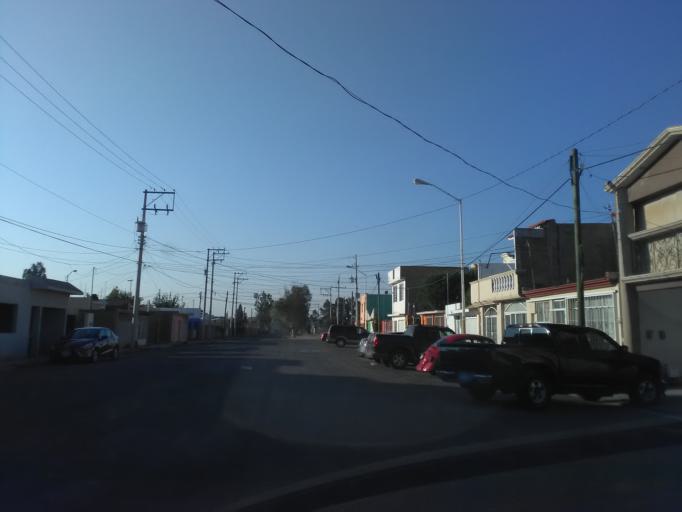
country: MX
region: Durango
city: Victoria de Durango
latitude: 24.0594
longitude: -104.6193
